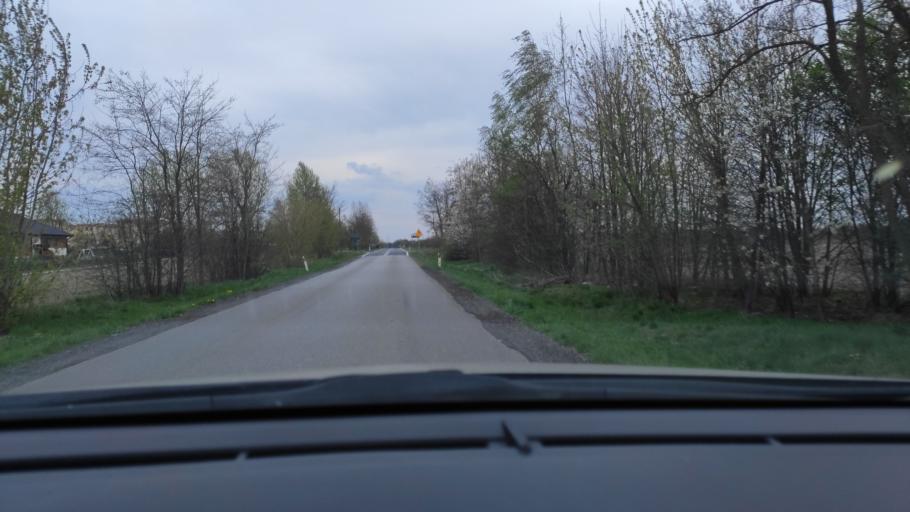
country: PL
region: Masovian Voivodeship
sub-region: Powiat zwolenski
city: Zwolen
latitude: 51.3655
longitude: 21.5643
